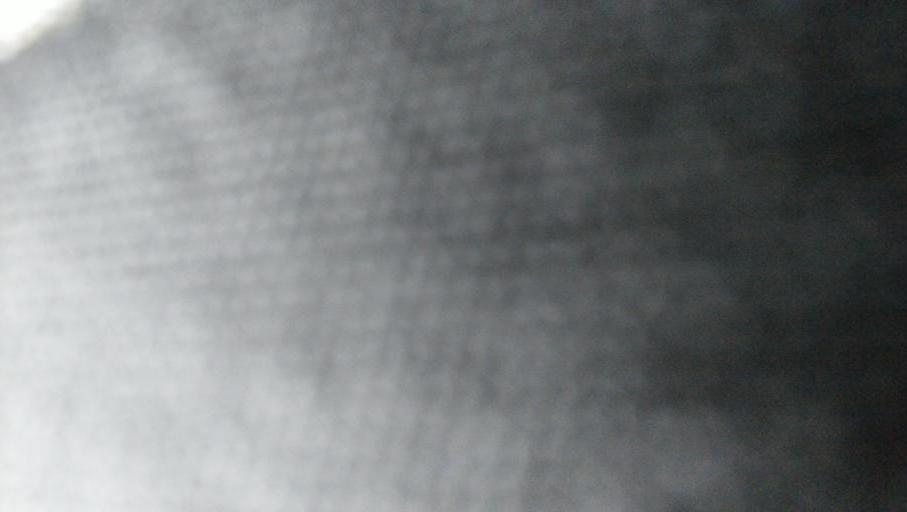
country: MX
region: Oaxaca
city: Juchitan de Zaragoza
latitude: 16.4495
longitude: -95.0232
